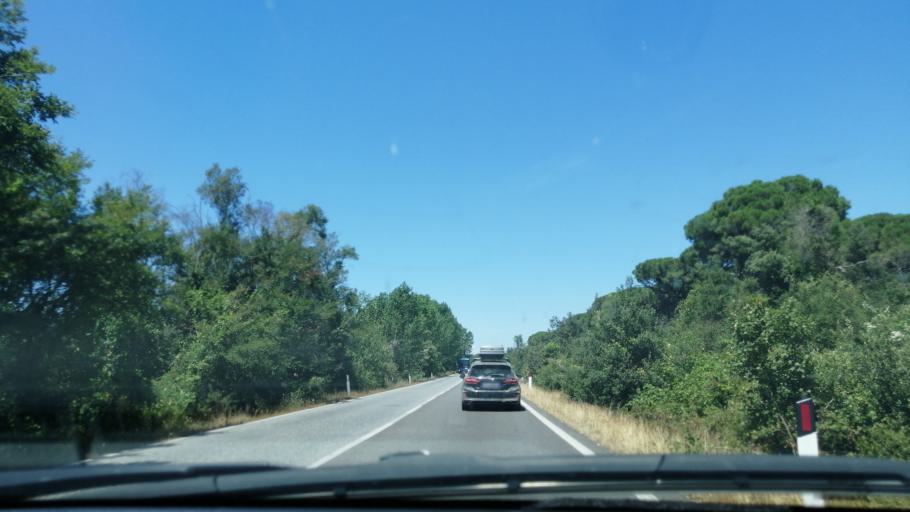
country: IT
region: Tuscany
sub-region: Province of Pisa
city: Migliarino
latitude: 43.7945
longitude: 10.3171
